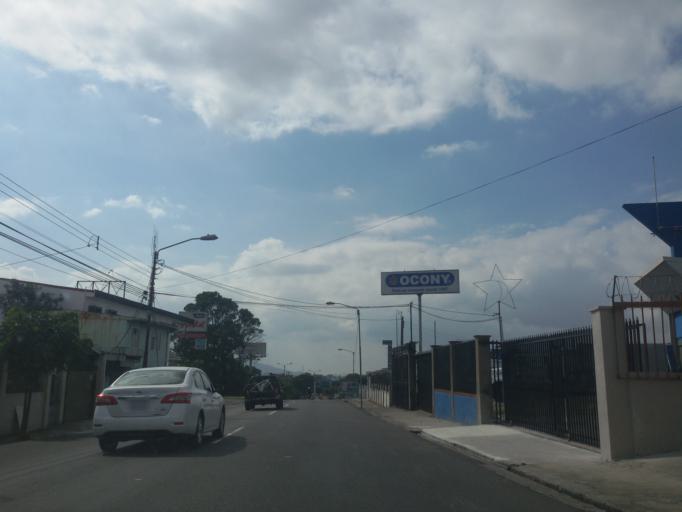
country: CR
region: San Jose
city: San Pedro
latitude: 9.9209
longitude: -84.0564
